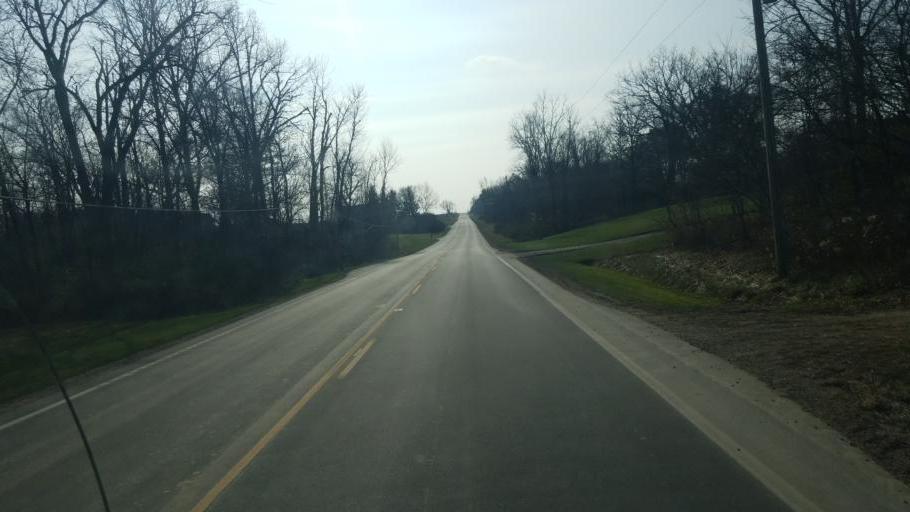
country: US
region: Ohio
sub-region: Mercer County
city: Fort Recovery
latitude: 40.4406
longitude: -84.7846
